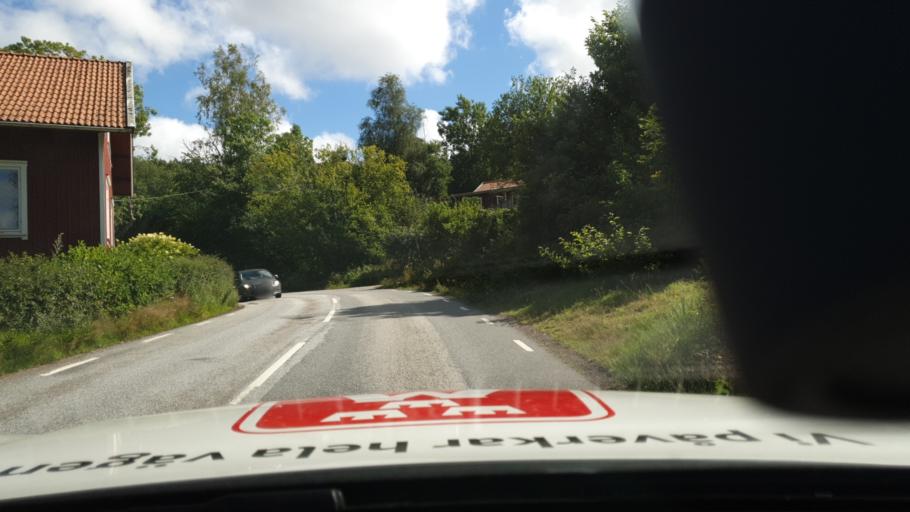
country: SE
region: Vaestra Goetaland
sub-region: Lysekils Kommun
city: Lysekil
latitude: 58.2010
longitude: 11.5426
